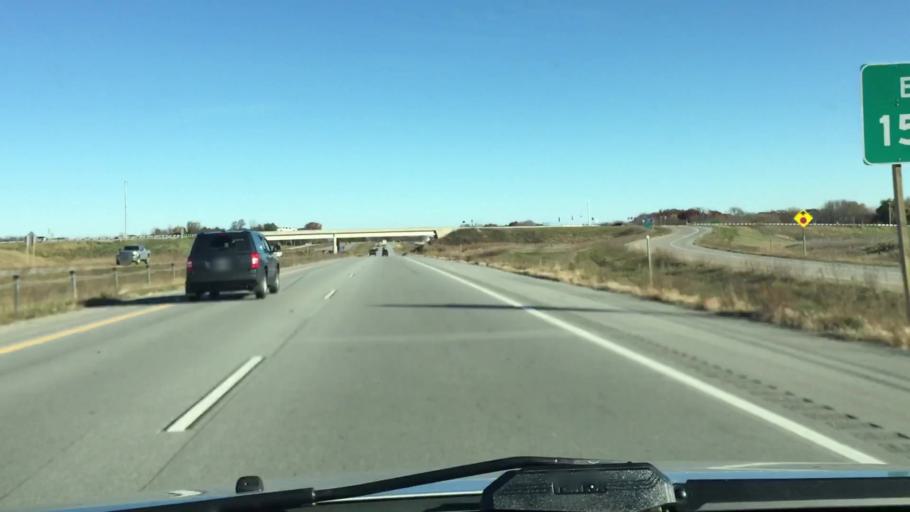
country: US
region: Wisconsin
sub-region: Brown County
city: Wrightstown
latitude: 44.3839
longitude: -88.1634
